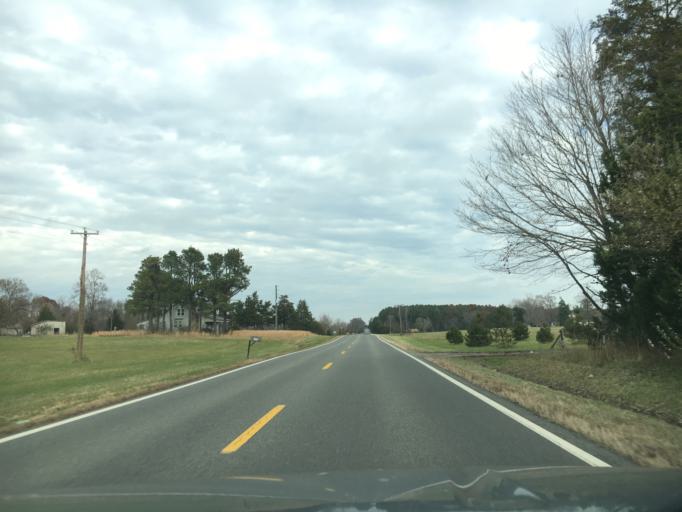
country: US
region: Virginia
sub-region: Cumberland County
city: Cumberland
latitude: 37.4467
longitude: -78.3216
